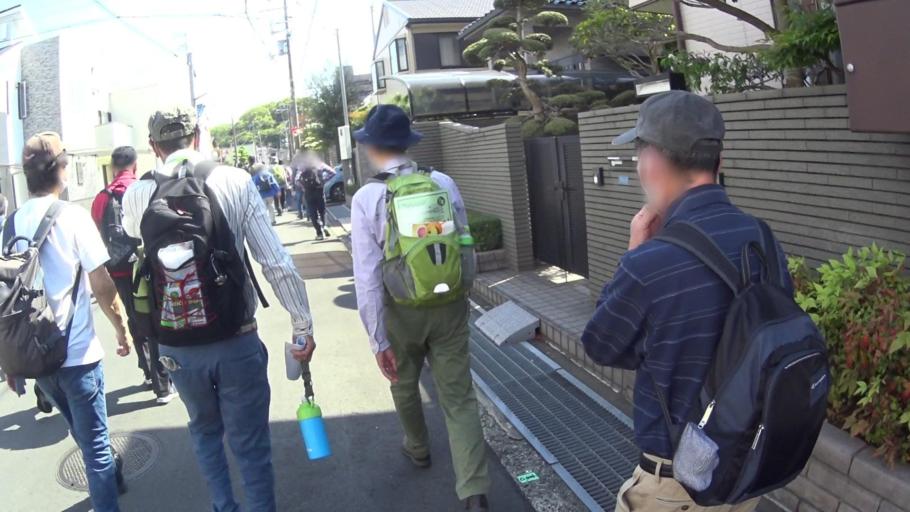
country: JP
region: Osaka
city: Kashihara
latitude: 34.5544
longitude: 135.6052
